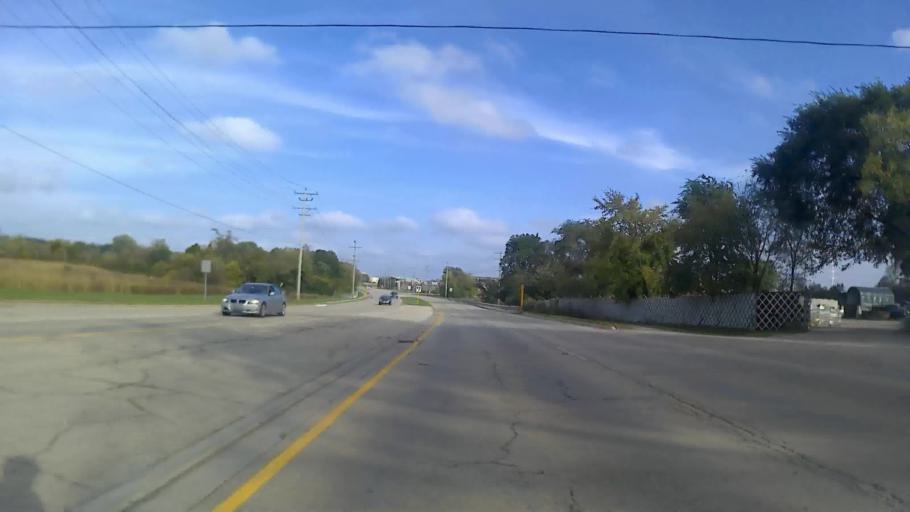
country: US
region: Illinois
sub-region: DuPage County
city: Warrenville
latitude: 41.8067
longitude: -88.1864
